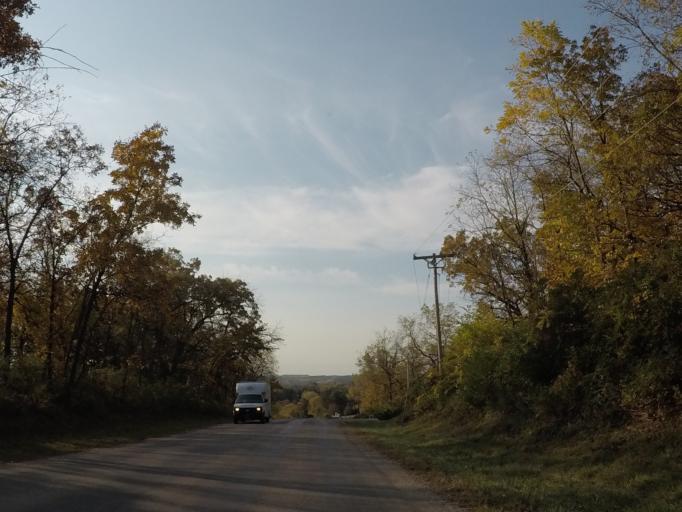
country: US
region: Wisconsin
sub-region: Dane County
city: Verona
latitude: 43.0429
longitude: -89.6015
